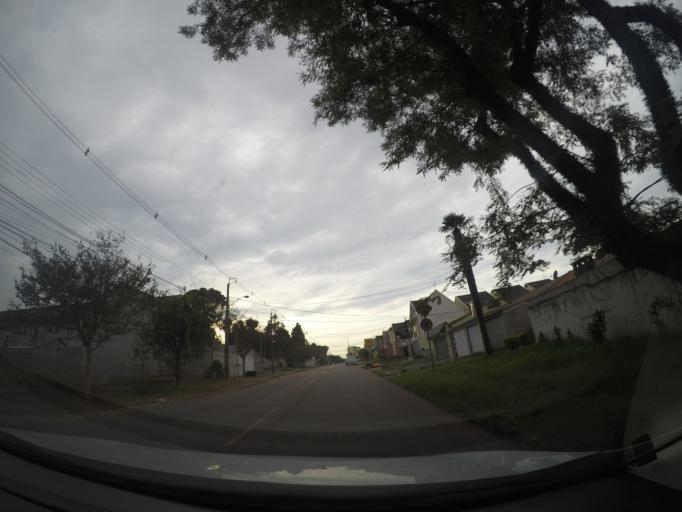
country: BR
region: Parana
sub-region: Sao Jose Dos Pinhais
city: Sao Jose dos Pinhais
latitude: -25.5168
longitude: -49.2383
